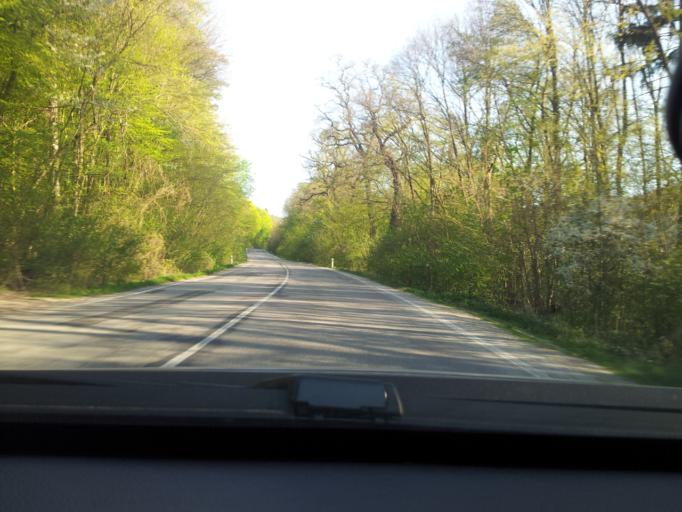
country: SK
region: Nitriansky
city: Zlate Moravce
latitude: 48.4357
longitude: 18.4113
